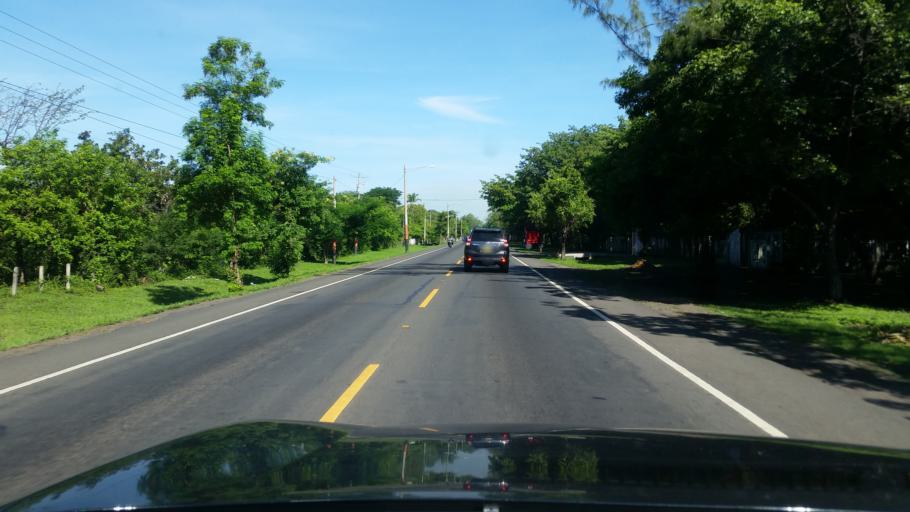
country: NI
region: Chinandega
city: Chichigalpa
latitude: 12.6079
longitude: -87.0685
